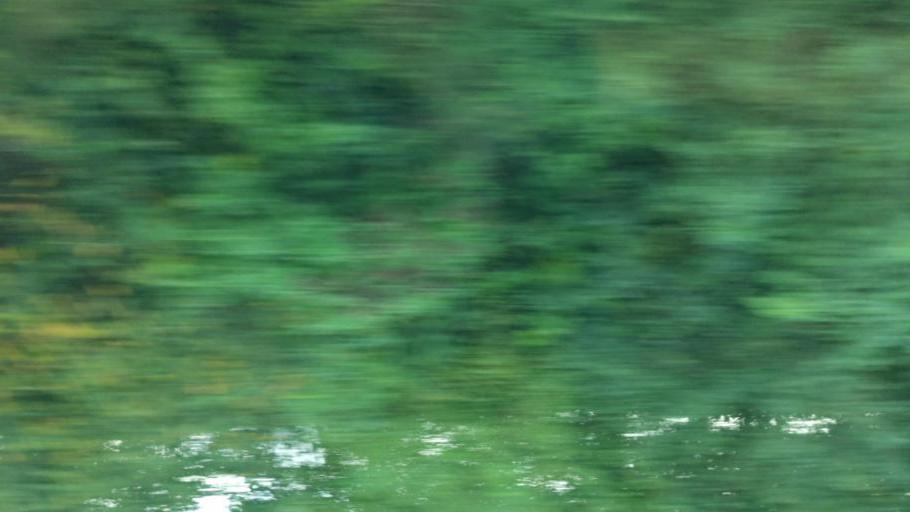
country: CZ
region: Central Bohemia
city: Uvaly
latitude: 50.0729
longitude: 14.7409
